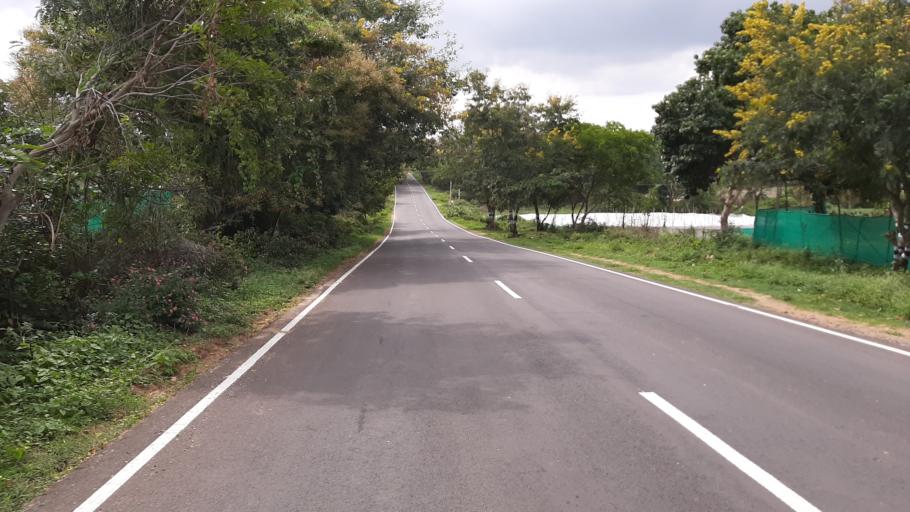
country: IN
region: Tamil Nadu
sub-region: Krishnagiri
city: Denkanikota
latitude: 12.5386
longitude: 77.7670
